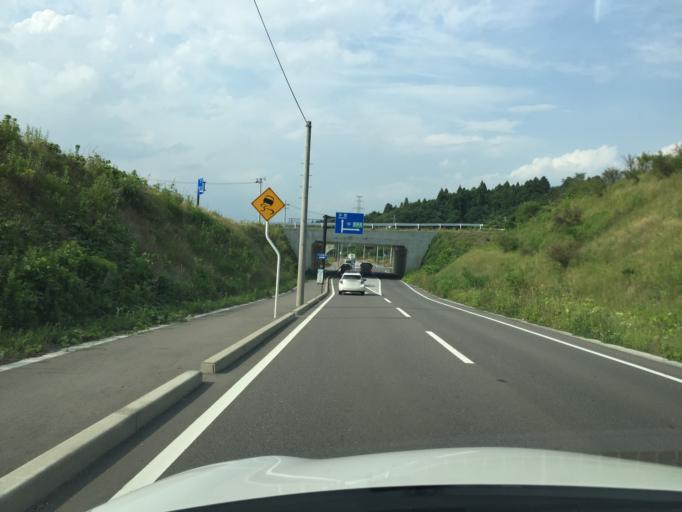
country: JP
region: Fukushima
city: Miharu
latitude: 37.4347
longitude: 140.4458
